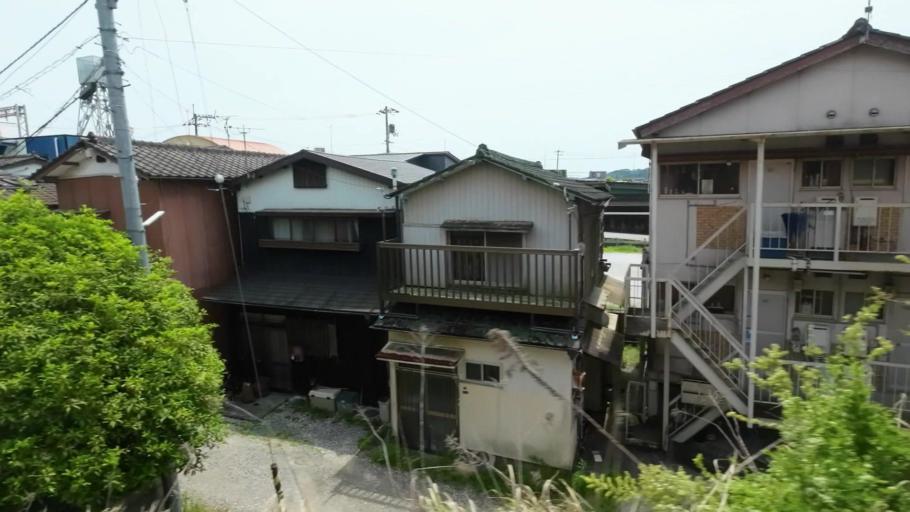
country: JP
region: Kochi
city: Kochi-shi
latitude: 33.5749
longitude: 133.5546
